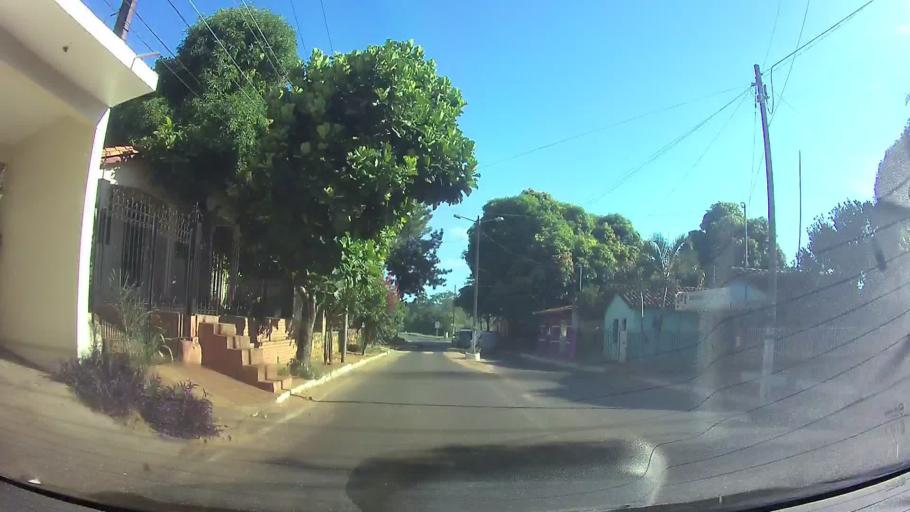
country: PY
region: Cordillera
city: Atyra
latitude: -25.2854
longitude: -57.1712
